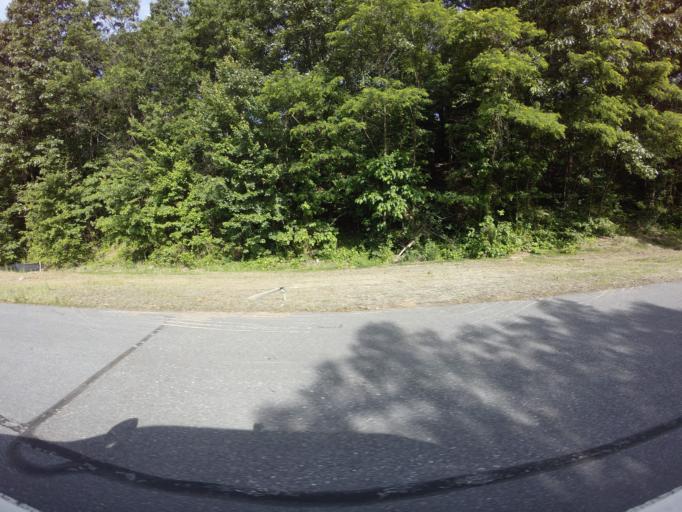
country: US
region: Maryland
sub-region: Frederick County
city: Green Valley
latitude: 39.3780
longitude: -77.2615
